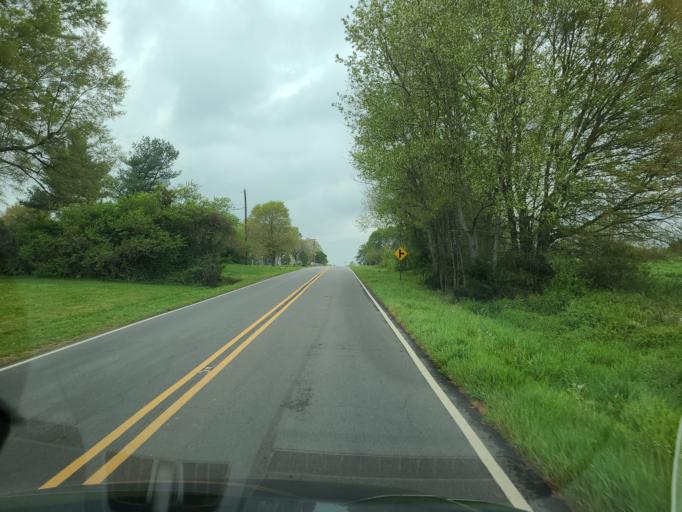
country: US
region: North Carolina
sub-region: Lincoln County
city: Lincolnton
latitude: 35.4607
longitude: -81.3241
